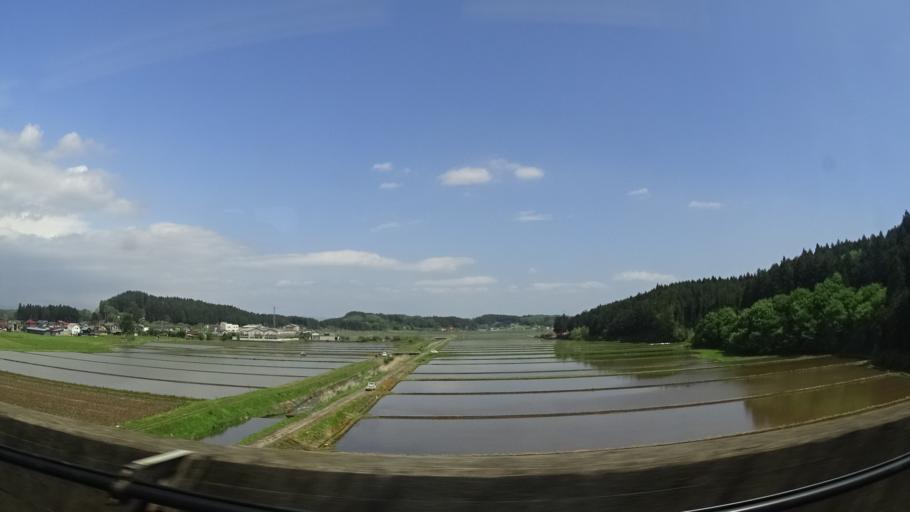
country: JP
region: Tochigi
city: Yaita
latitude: 36.8161
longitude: 139.9587
